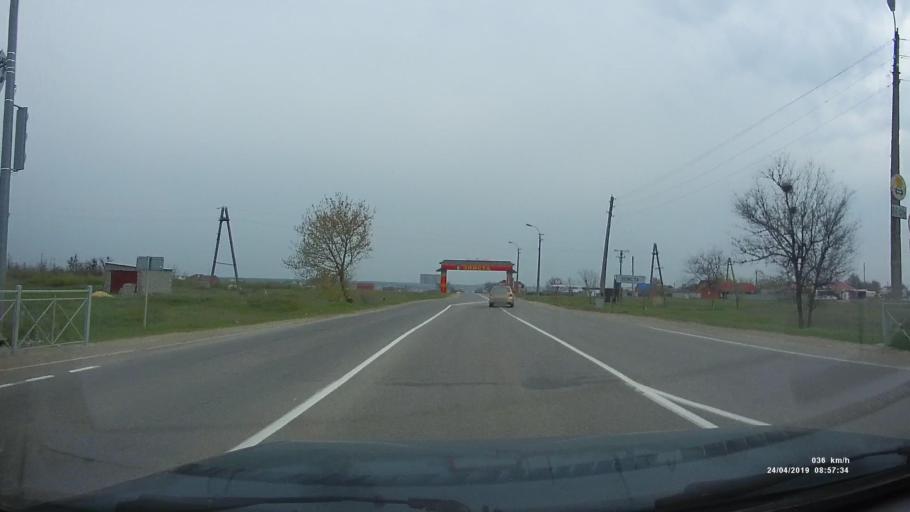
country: RU
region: Kalmykiya
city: Arshan'
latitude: 46.3034
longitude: 44.1888
